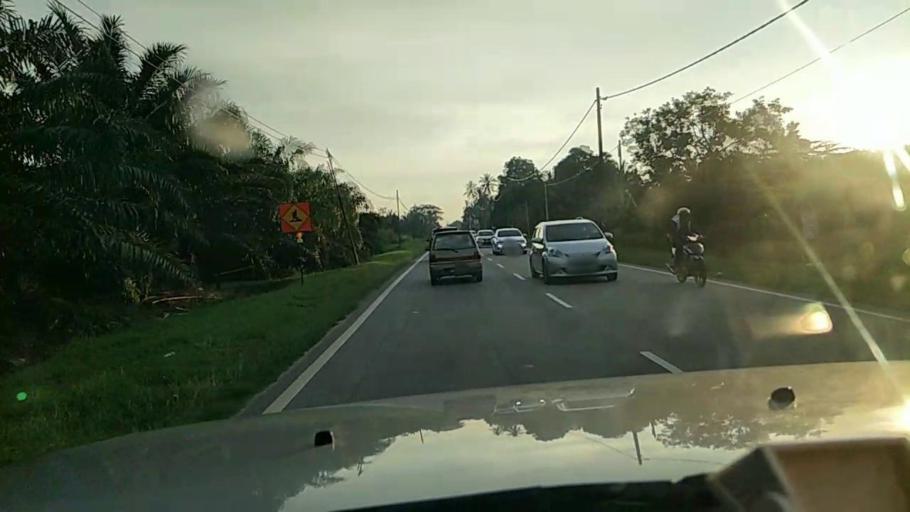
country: MY
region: Selangor
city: Kuala Selangor
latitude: 3.3036
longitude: 101.3000
